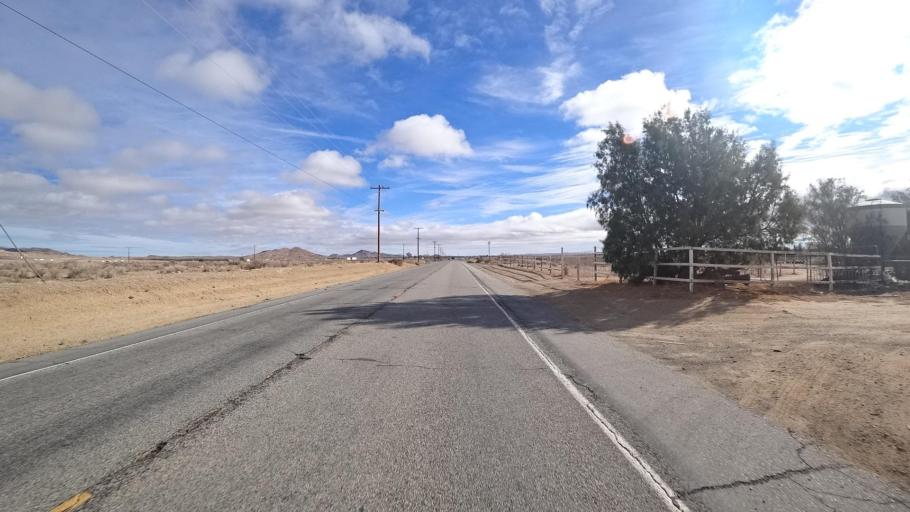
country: US
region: California
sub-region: Kern County
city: Rosamond
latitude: 34.8636
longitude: -118.2760
